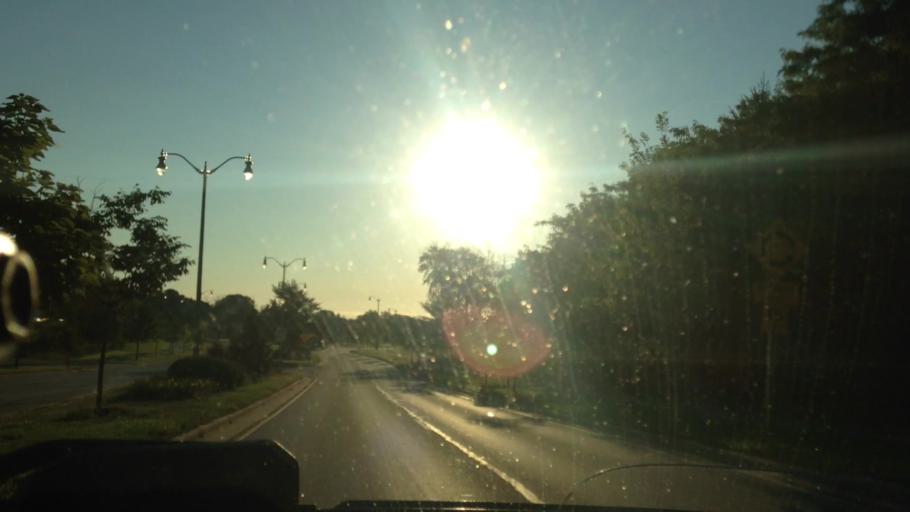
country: US
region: Wisconsin
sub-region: Ozaukee County
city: Port Washington
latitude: 43.3869
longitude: -87.9029
